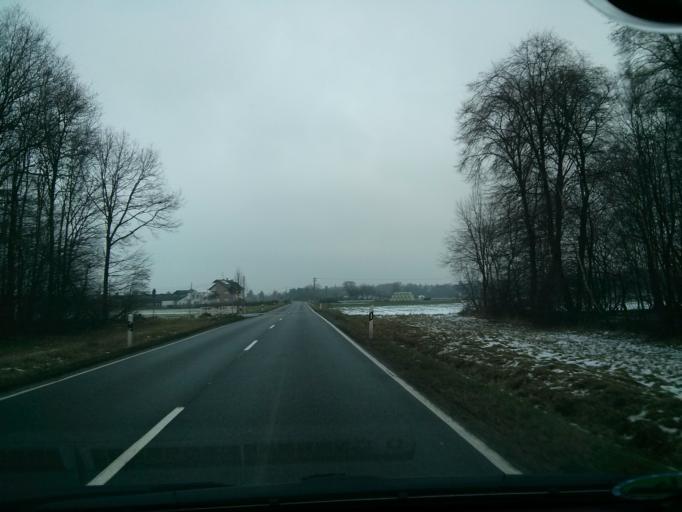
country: DE
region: North Rhine-Westphalia
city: Meckenheim
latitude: 50.6699
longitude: 7.0149
